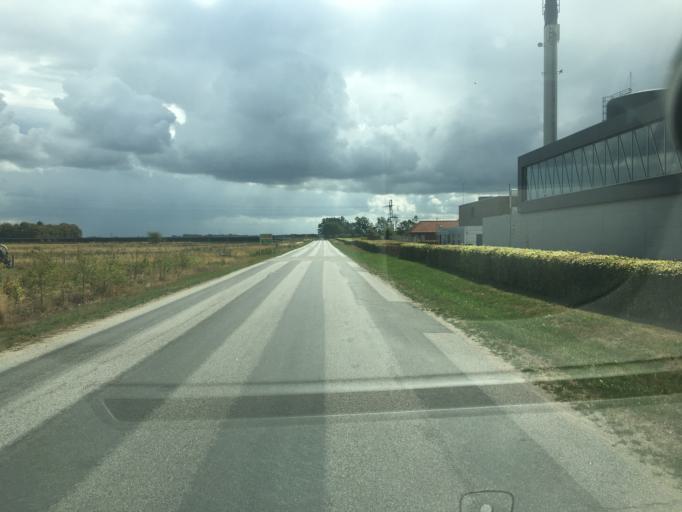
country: DK
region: South Denmark
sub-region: Tonder Kommune
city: Logumkloster
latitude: 55.0531
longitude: 8.9581
